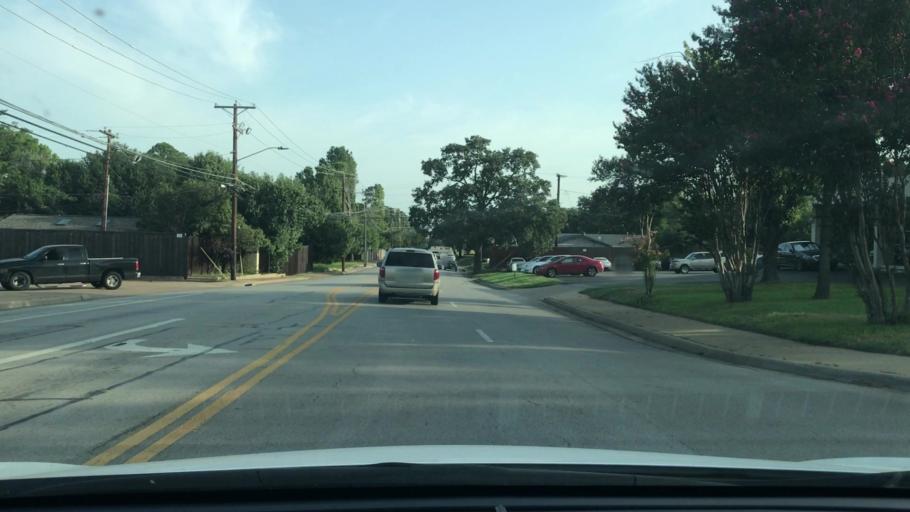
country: US
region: Texas
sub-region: Tarrant County
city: Arlington
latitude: 32.7503
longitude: -97.1232
